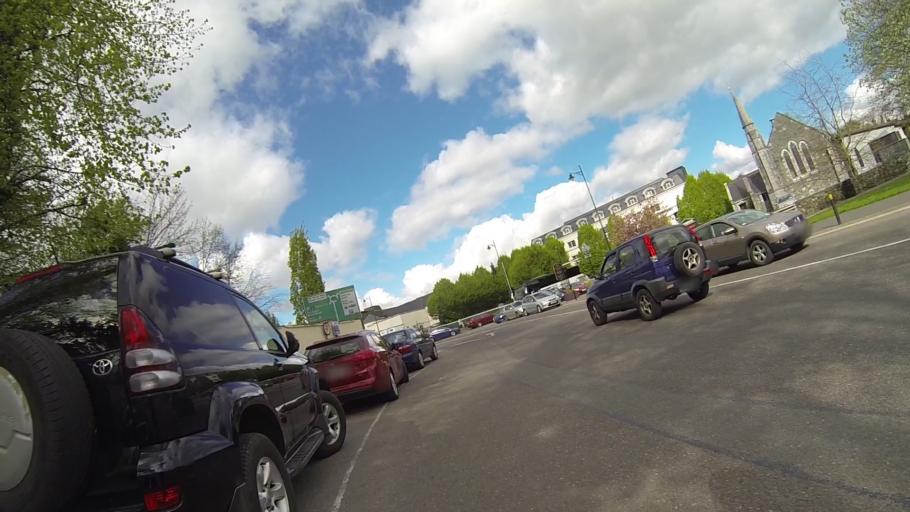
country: IE
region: Munster
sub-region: Ciarrai
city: Cill Airne
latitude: 52.0570
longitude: -9.5071
